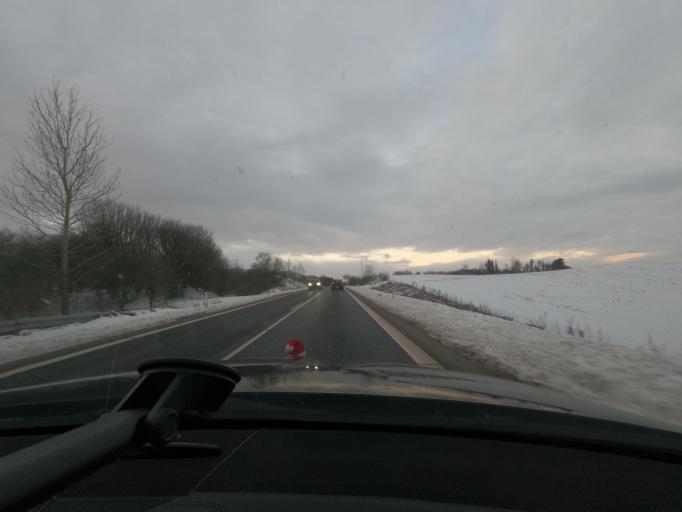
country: DK
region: South Denmark
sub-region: Aabenraa Kommune
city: Krusa
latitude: 54.8640
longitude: 9.4509
